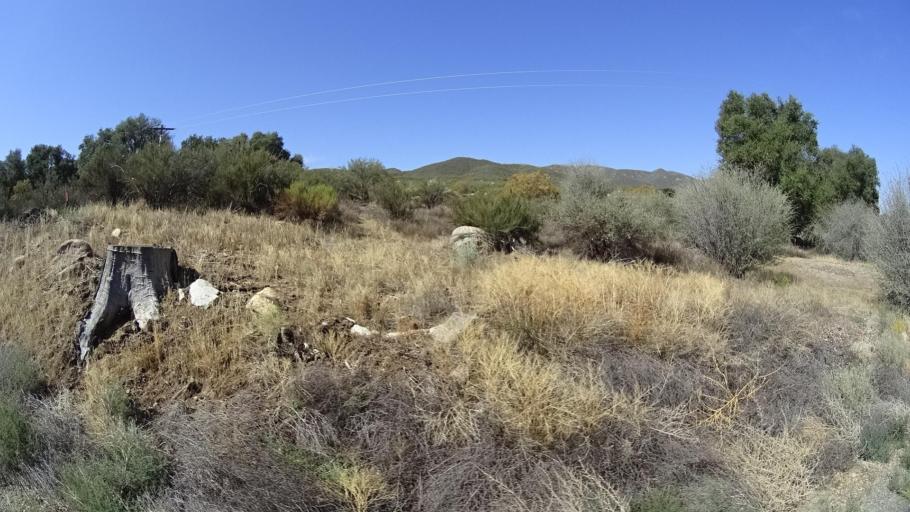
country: US
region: California
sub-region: Riverside County
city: Aguanga
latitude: 33.3363
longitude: -116.7175
